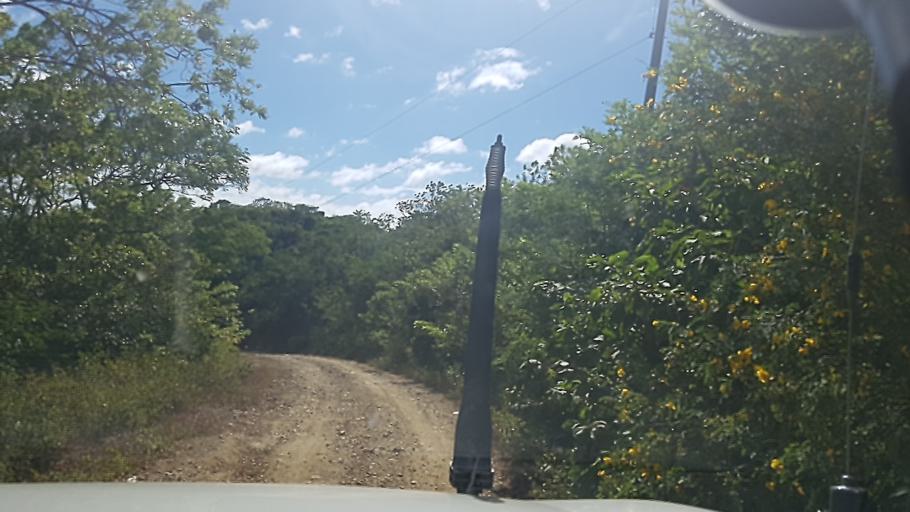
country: NI
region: Carazo
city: Santa Teresa
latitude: 11.6110
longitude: -86.1549
